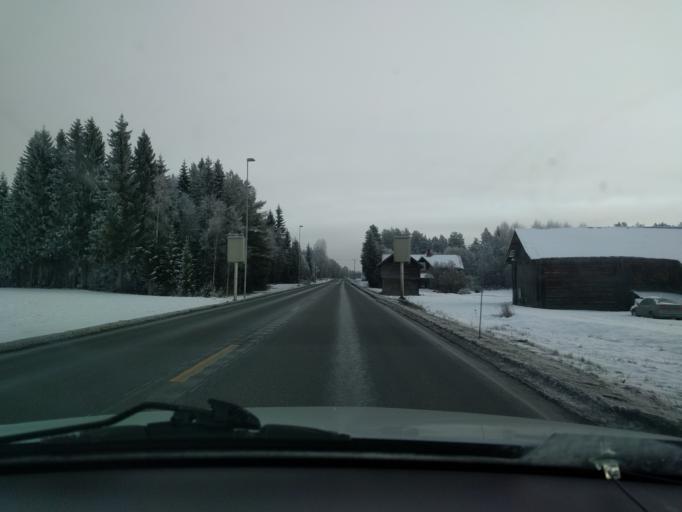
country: NO
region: Hedmark
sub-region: Loten
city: Loten
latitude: 60.8563
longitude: 11.3911
